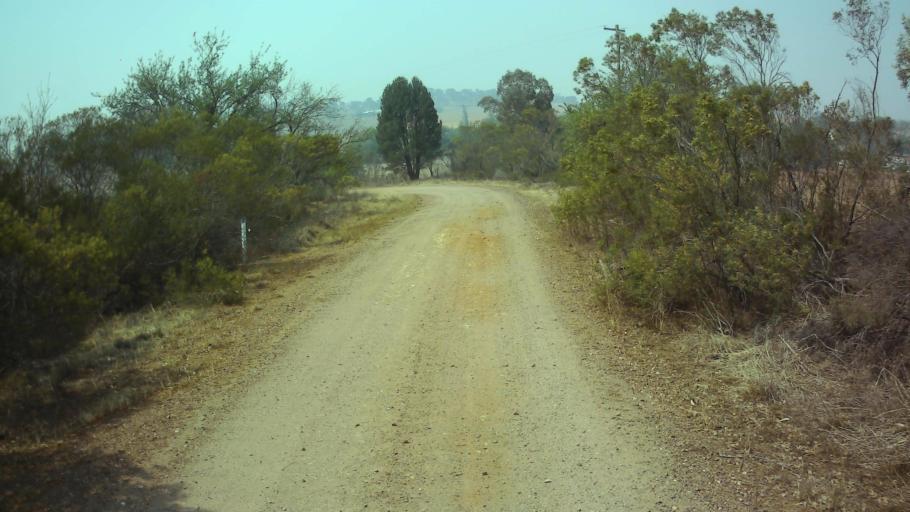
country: AU
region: New South Wales
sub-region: Weddin
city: Grenfell
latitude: -33.9047
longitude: 148.1729
